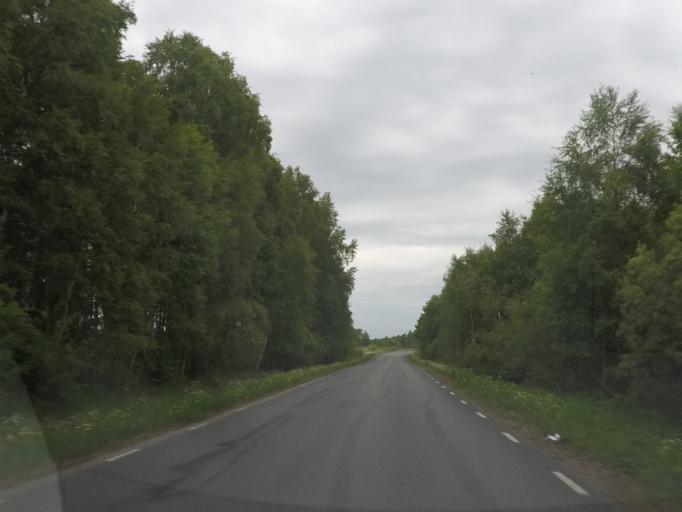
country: SE
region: Soedermanland
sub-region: Eskilstuna Kommun
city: Arla
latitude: 59.2653
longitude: 16.6571
